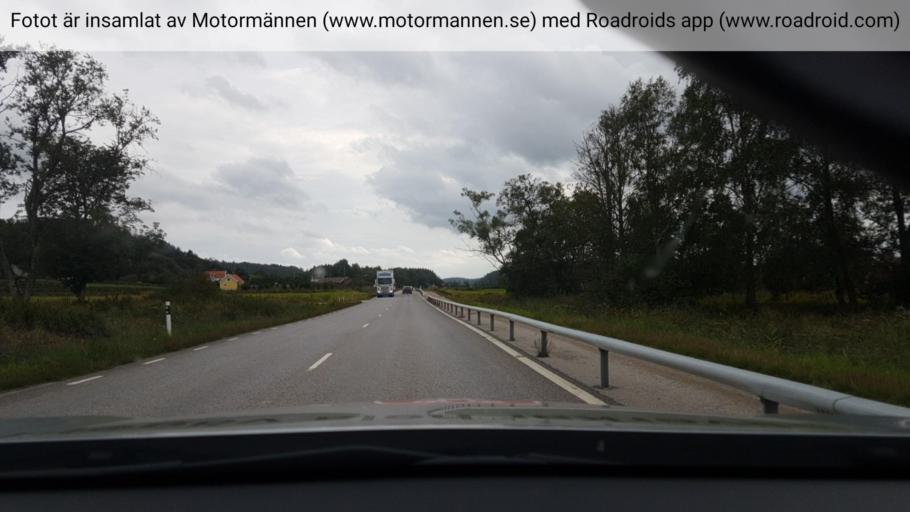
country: SE
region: Vaestra Goetaland
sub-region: Munkedals Kommun
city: Munkedal
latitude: 58.5110
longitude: 11.5756
